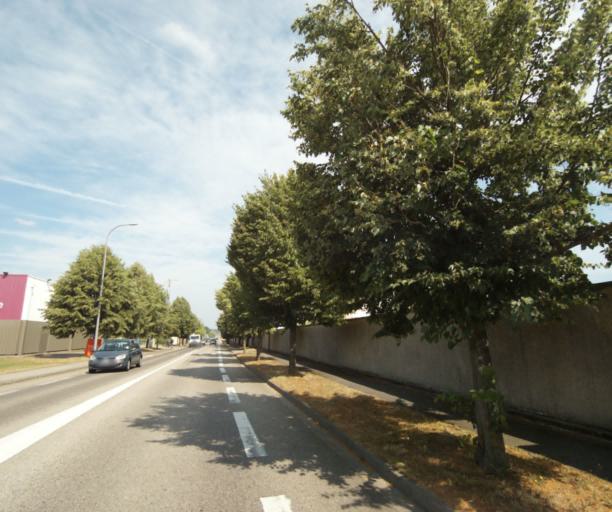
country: FR
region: Lorraine
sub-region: Departement de Meurthe-et-Moselle
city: Chanteheux
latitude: 48.5811
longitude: 6.5187
